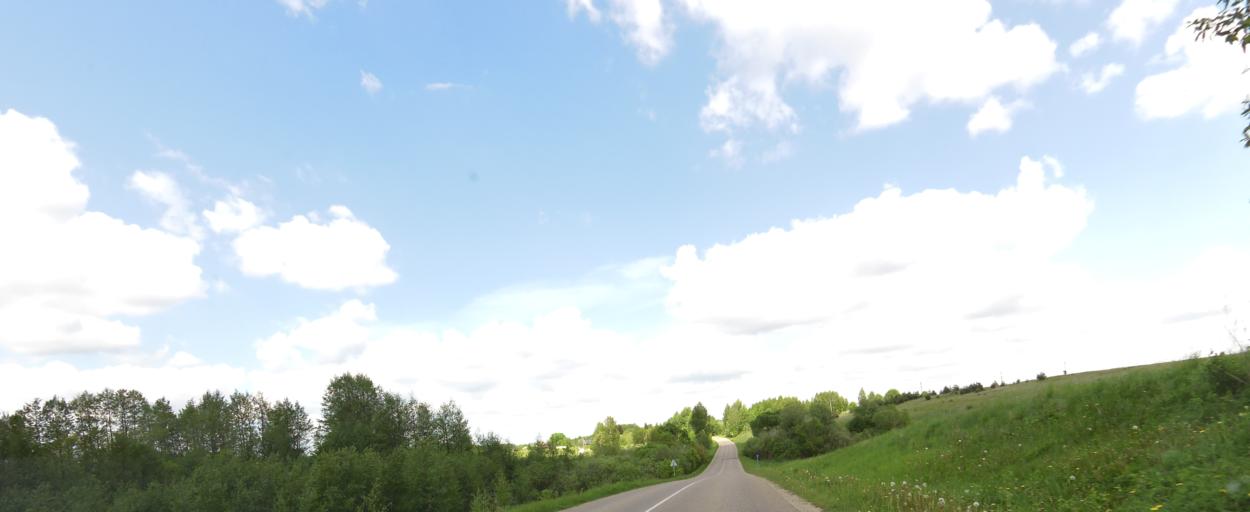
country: LT
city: Trakai
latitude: 54.6825
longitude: 24.9553
